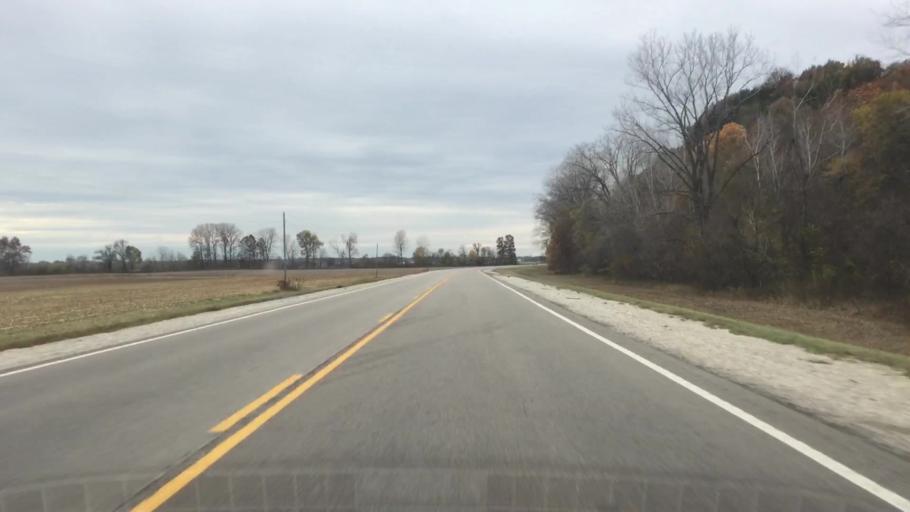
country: US
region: Missouri
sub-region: Callaway County
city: Holts Summit
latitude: 38.5835
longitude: -92.1126
